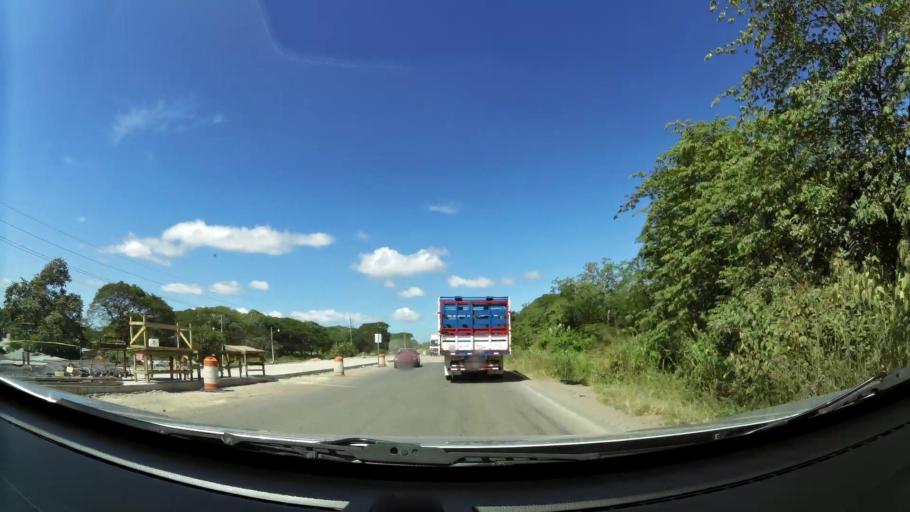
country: CR
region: Guanacaste
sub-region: Canton de Canas
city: Canas
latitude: 10.4536
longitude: -85.1303
